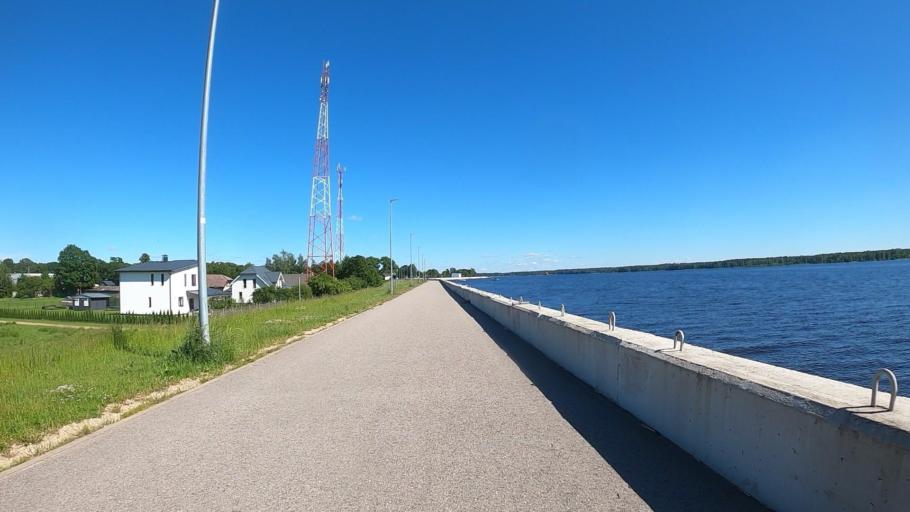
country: LV
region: Ikskile
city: Ikskile
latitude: 56.8313
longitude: 24.4793
